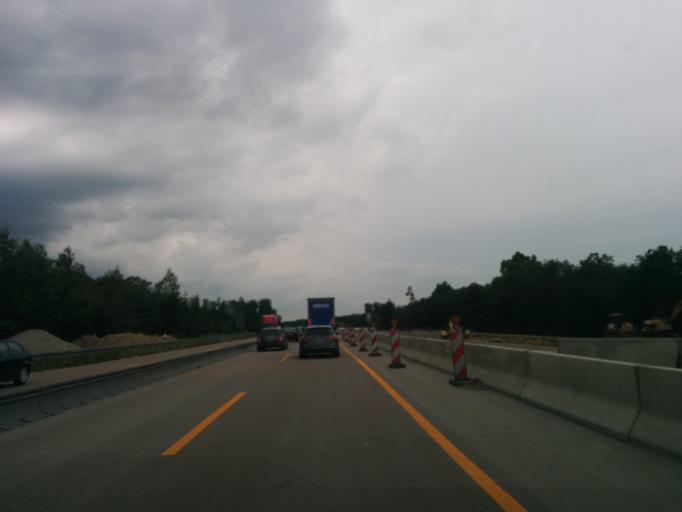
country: DE
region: Bavaria
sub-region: Swabia
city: Landensberg
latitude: 48.4055
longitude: 10.5214
